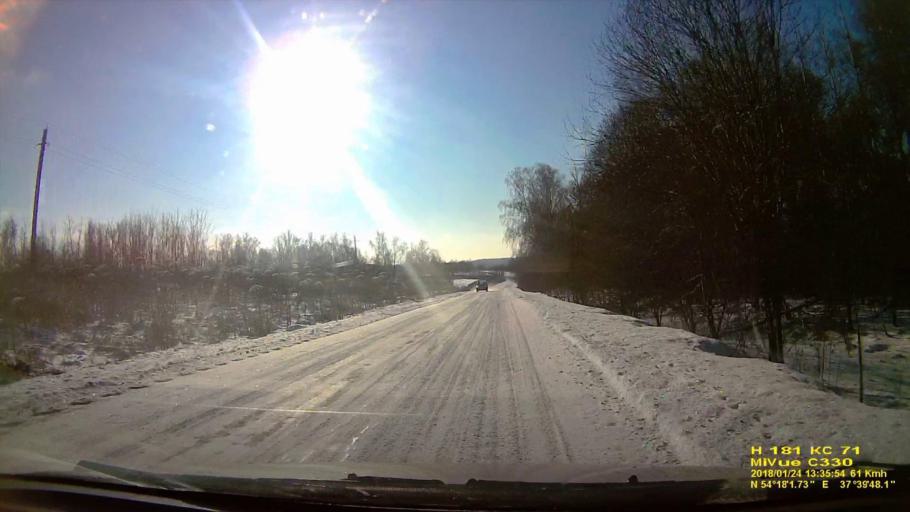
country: RU
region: Tula
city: Revyakino
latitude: 54.3003
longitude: 37.6632
